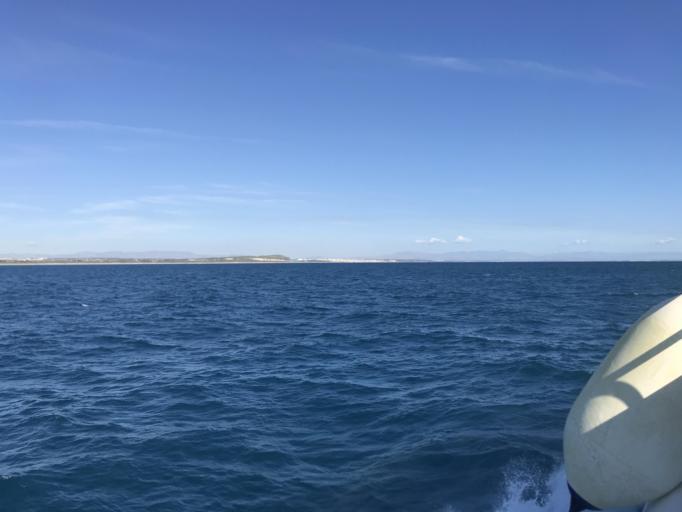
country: ES
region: Valencia
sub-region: Provincia de Alicante
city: Torrevieja
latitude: 38.0144
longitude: -0.6262
